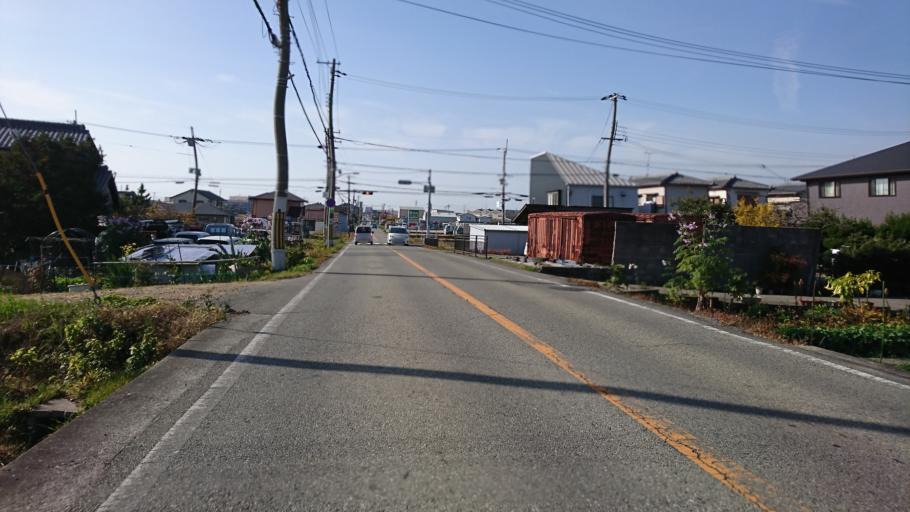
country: JP
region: Hyogo
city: Kakogawacho-honmachi
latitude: 34.7312
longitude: 134.8729
